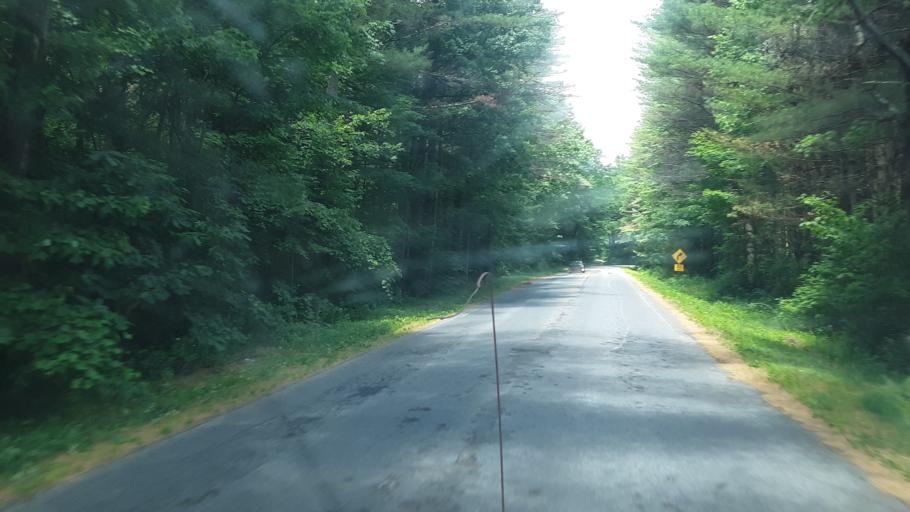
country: US
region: New York
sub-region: Oneida County
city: Rome
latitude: 43.2560
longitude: -75.5962
